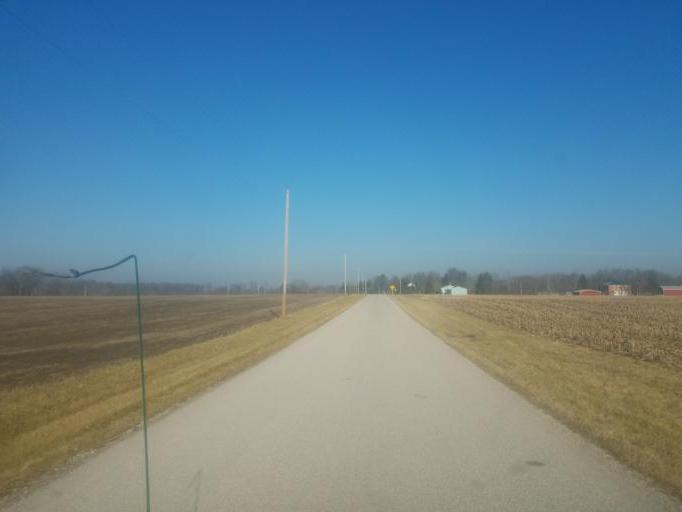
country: US
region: Ohio
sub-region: Seneca County
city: Tiffin
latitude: 41.1211
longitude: -83.1120
